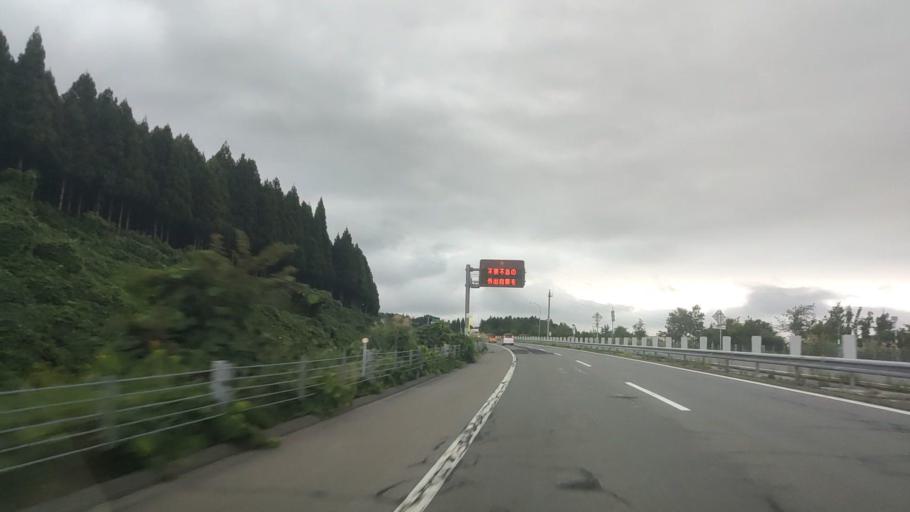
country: JP
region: Hokkaido
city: Nanae
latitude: 41.9029
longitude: 140.6993
